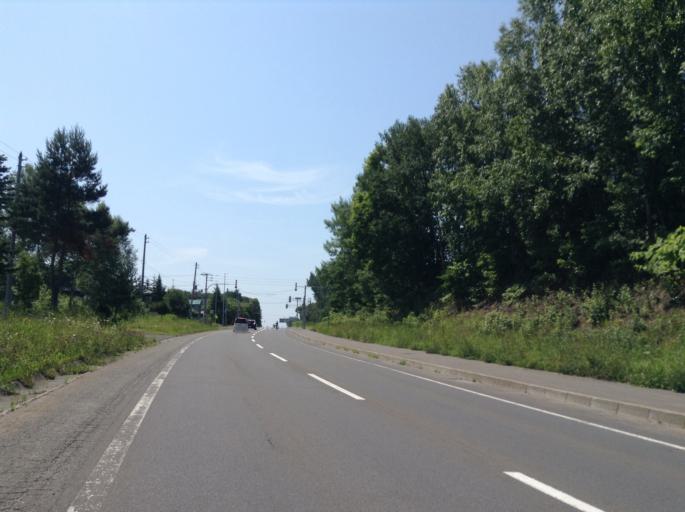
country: JP
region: Hokkaido
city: Nayoro
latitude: 44.3479
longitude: 142.4746
